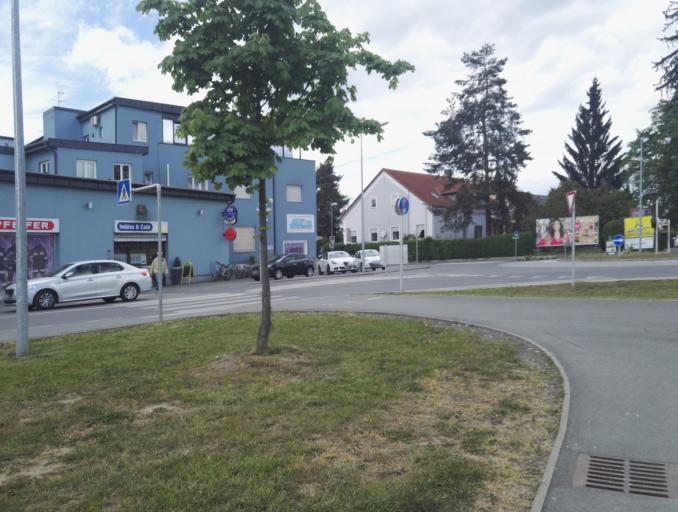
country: AT
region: Styria
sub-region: Politischer Bezirk Leibnitz
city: Leibnitz
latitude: 46.7819
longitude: 15.5462
